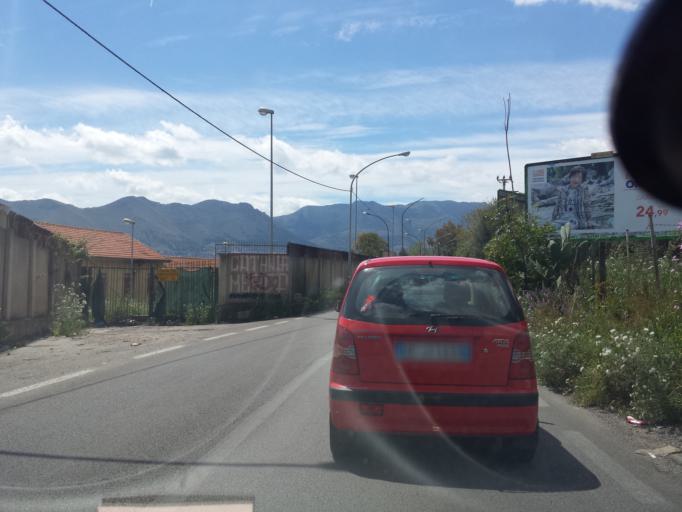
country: IT
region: Sicily
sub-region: Palermo
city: Monreale
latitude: 38.1019
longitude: 13.3105
